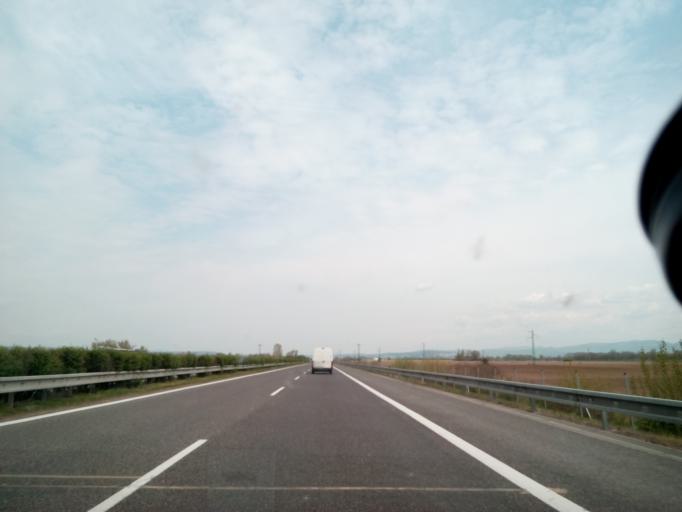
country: SK
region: Trenciansky
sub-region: Okres Nove Mesto nad Vahom
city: Nove Mesto nad Vahom
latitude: 48.8247
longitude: 17.9158
